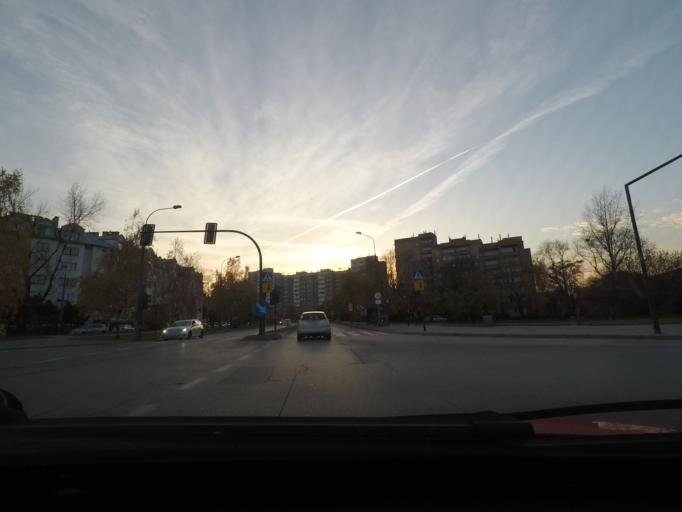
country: PL
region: Lesser Poland Voivodeship
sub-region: Krakow
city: Krakow
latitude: 50.0281
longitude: 19.9148
